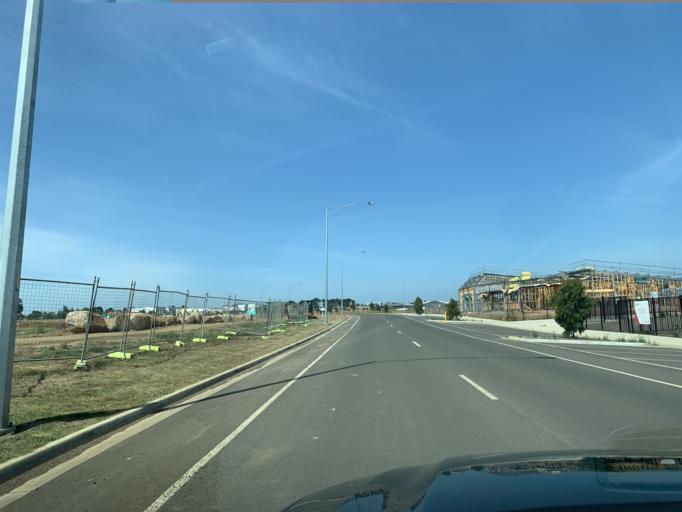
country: AU
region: Victoria
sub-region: Ballarat North
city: Newington
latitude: -37.5460
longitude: 143.7797
